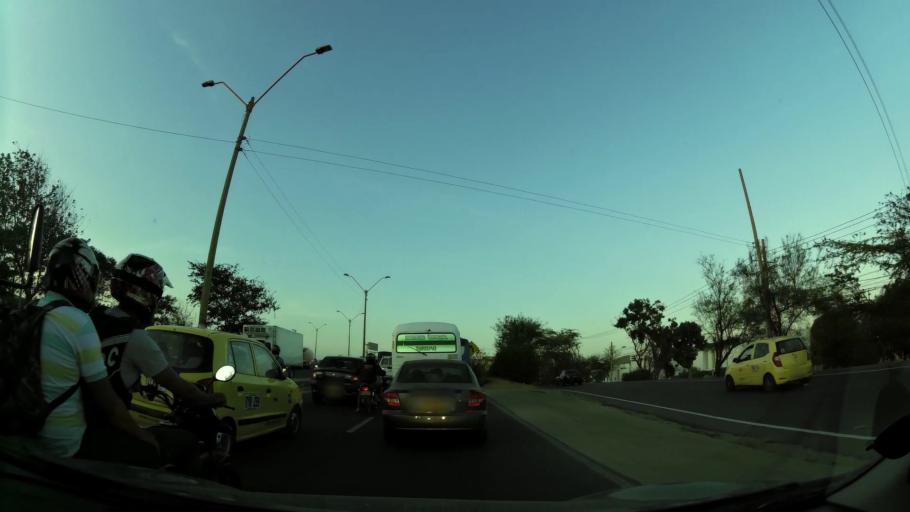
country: CO
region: Atlantico
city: Soledad
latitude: 10.9331
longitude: -74.7802
